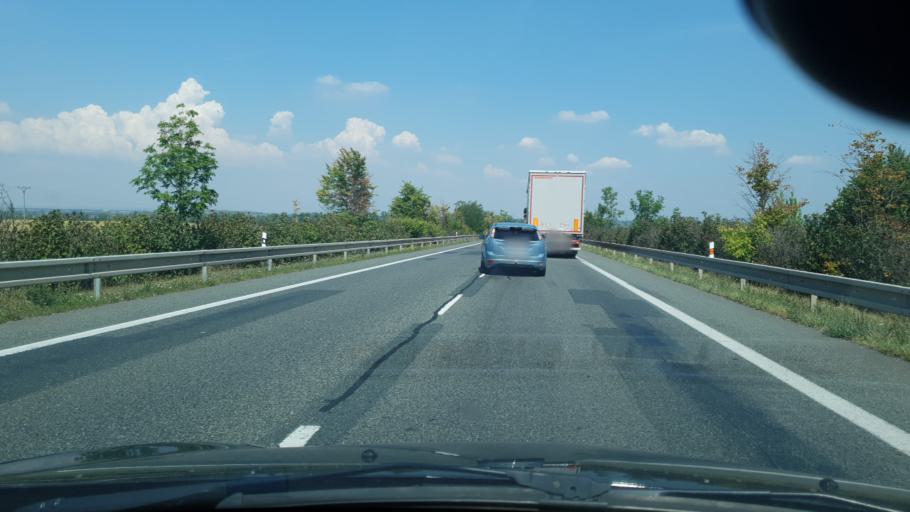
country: CZ
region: South Moravian
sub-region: Okres Breclav
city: Dolni Dunajovice
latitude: 48.8687
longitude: 16.6064
